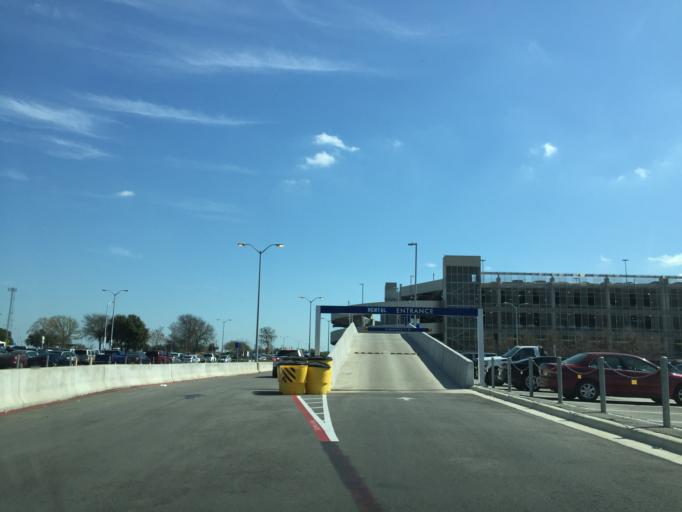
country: US
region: Texas
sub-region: Travis County
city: Hornsby Bend
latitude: 30.2054
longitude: -97.6683
